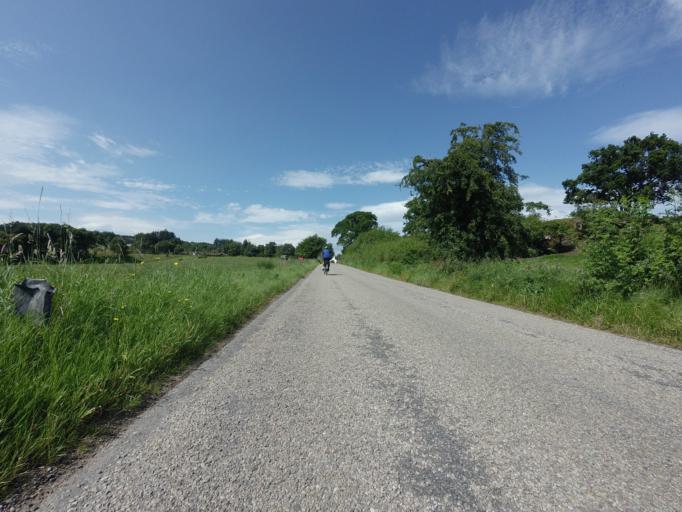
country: GB
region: Scotland
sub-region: Highland
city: Inverness
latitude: 57.5227
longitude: -4.3100
